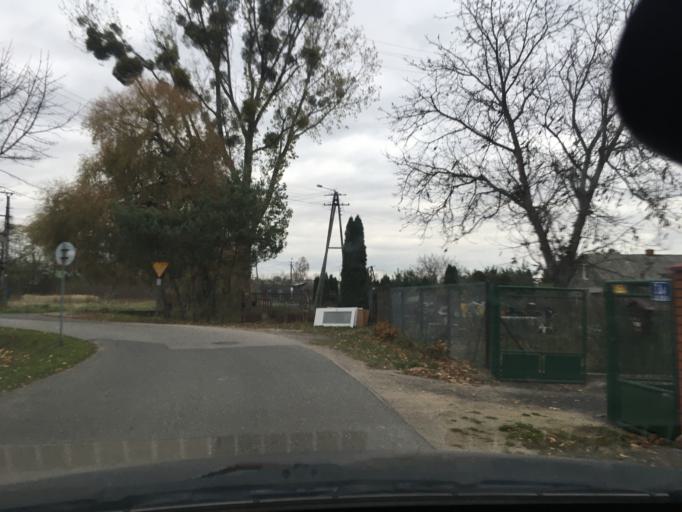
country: PL
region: Lodz Voivodeship
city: Zabia Wola
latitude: 52.0324
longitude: 20.6922
